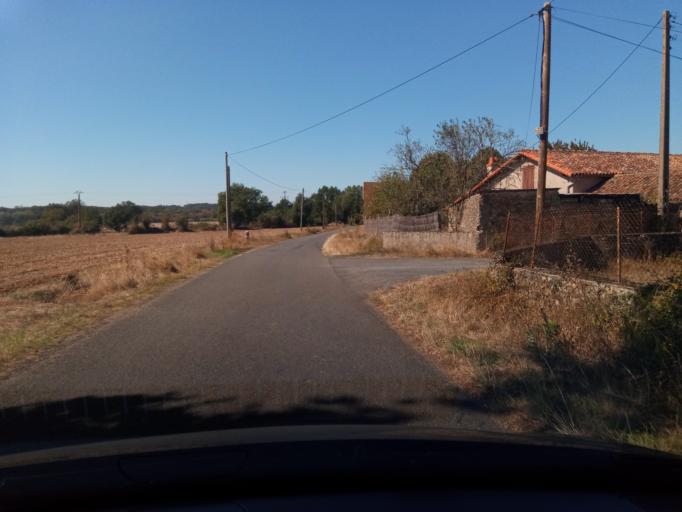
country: FR
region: Poitou-Charentes
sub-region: Departement de la Vienne
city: Montmorillon
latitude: 46.4818
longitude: 0.8515
